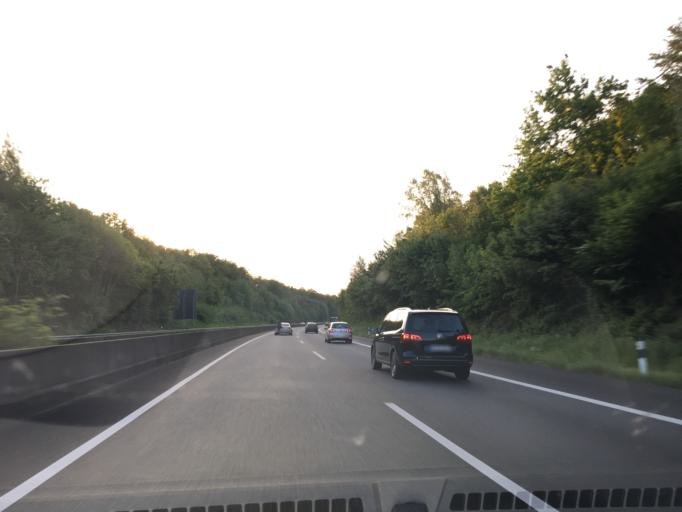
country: DE
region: Lower Saxony
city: Osnabrueck
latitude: 52.2471
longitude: 8.0261
